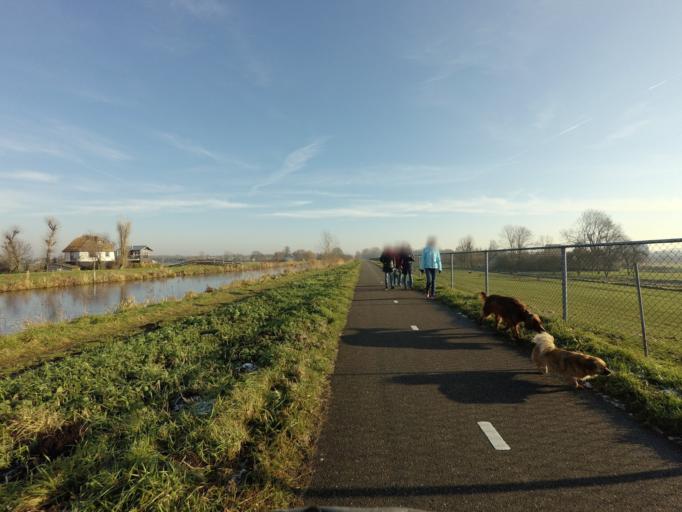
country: NL
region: Utrecht
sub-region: Gemeente De Ronde Venen
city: Mijdrecht
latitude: 52.2113
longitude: 4.8492
